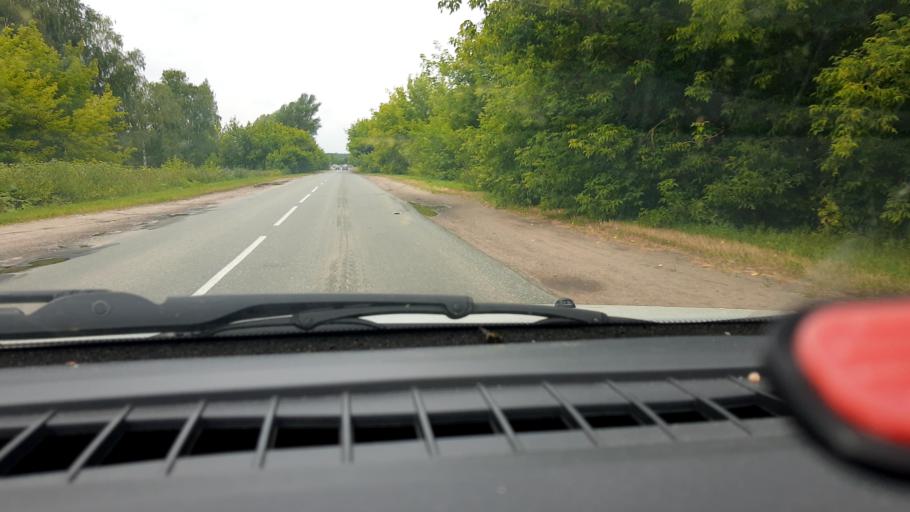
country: RU
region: Nizjnij Novgorod
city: Kstovo
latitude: 56.1338
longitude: 44.0960
